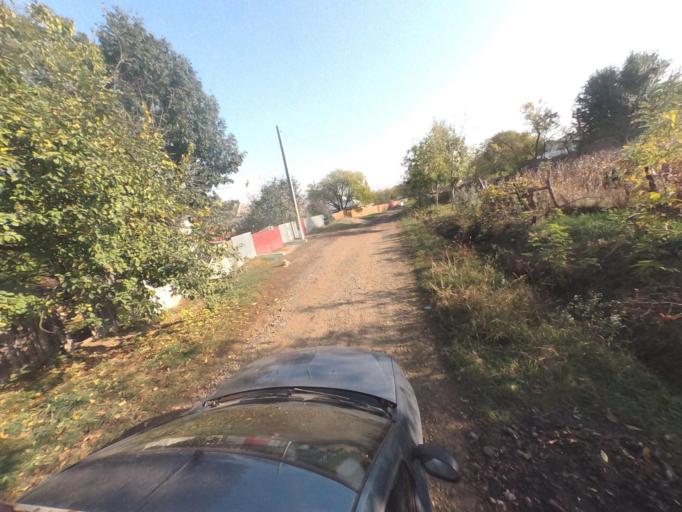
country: RO
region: Vaslui
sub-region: Comuna Bacesti
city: Bacesti
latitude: 46.8757
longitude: 27.1951
